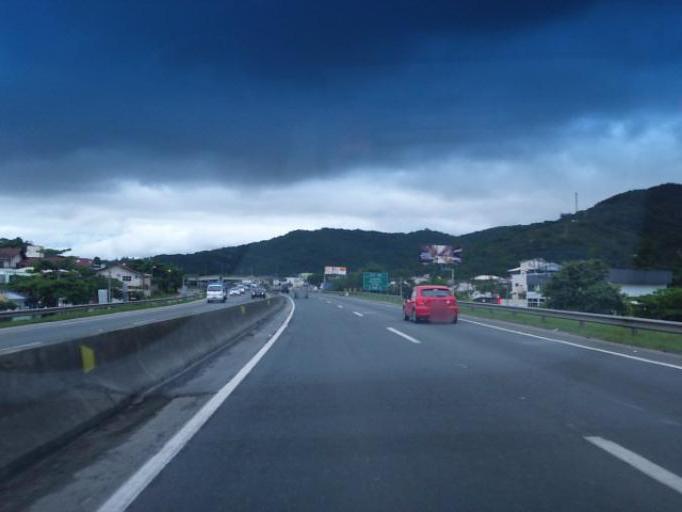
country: BR
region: Santa Catarina
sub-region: Itapema
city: Itapema
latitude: -27.0955
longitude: -48.6183
